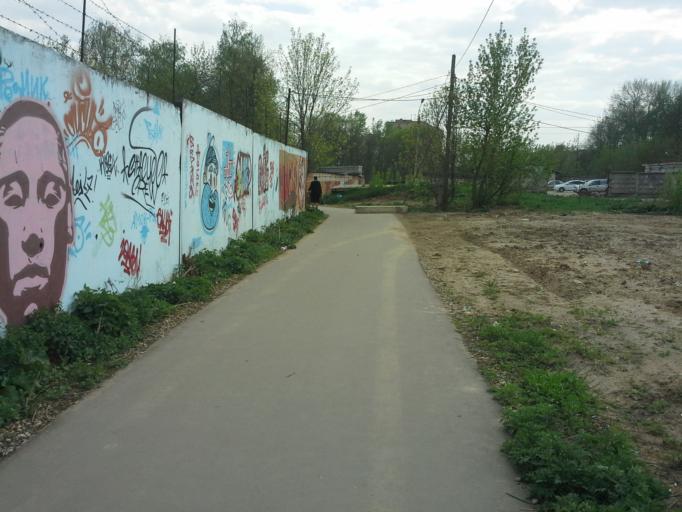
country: RU
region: Moskovskaya
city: Sergiyev Posad
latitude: 56.3168
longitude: 38.1440
